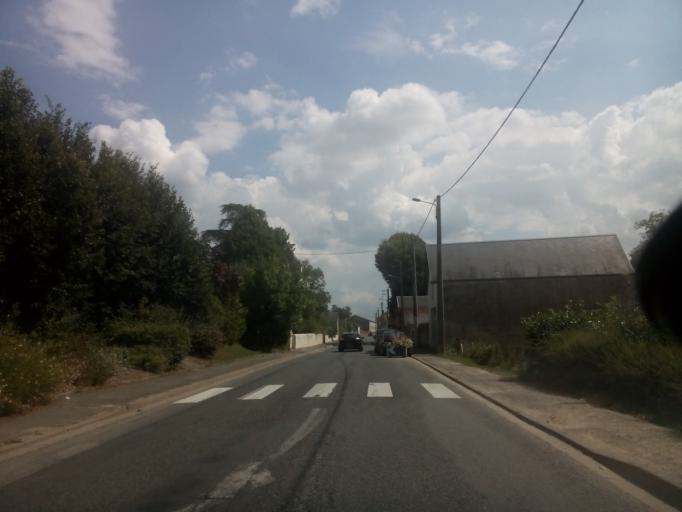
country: FR
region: Centre
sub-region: Departement d'Indre-et-Loire
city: Azay-le-Rideau
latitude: 47.2644
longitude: 0.4499
